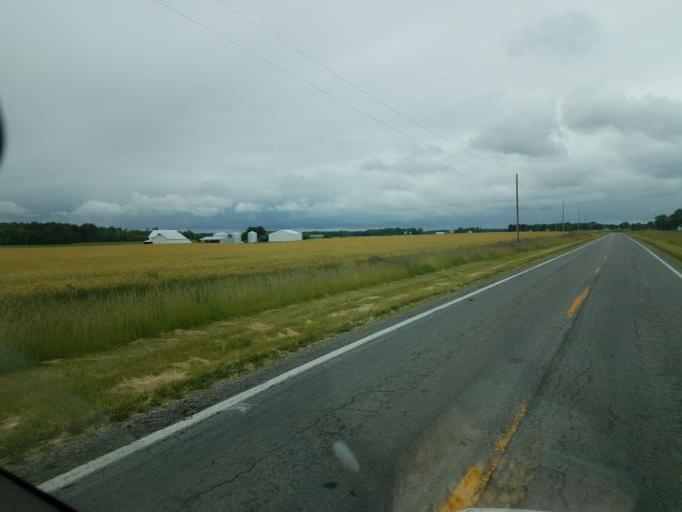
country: US
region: Ohio
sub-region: Marion County
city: Marion
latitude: 40.5478
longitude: -83.0338
